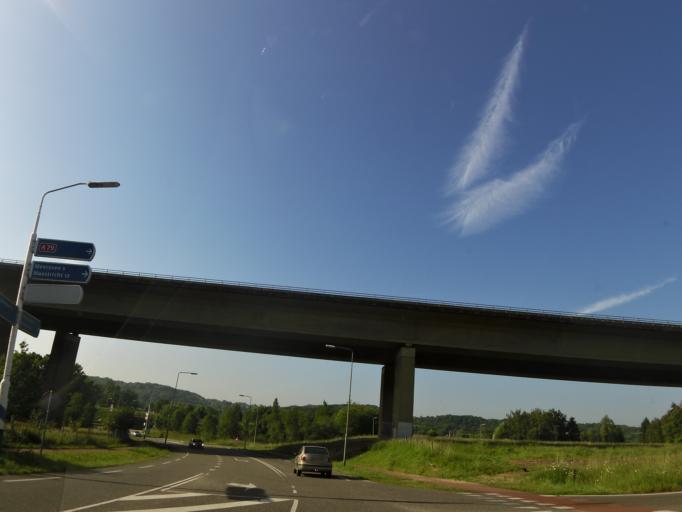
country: NL
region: Limburg
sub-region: Valkenburg aan de Geul
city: Broekhem
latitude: 50.8750
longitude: 5.8131
